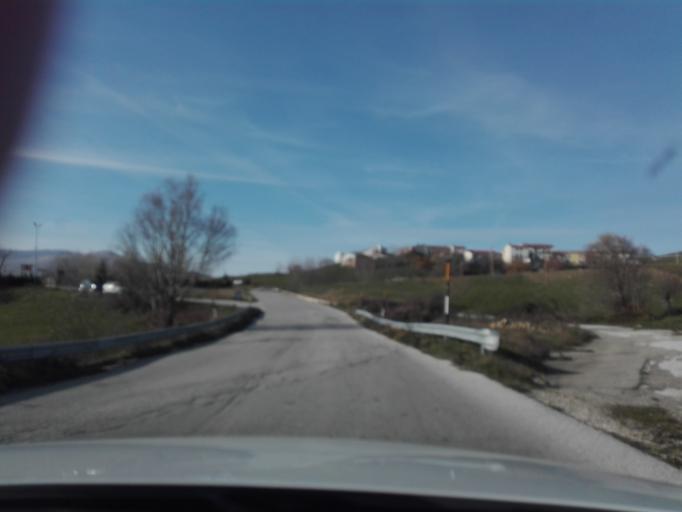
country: IT
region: Molise
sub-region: Provincia di Isernia
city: Agnone
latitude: 41.8391
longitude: 14.3759
